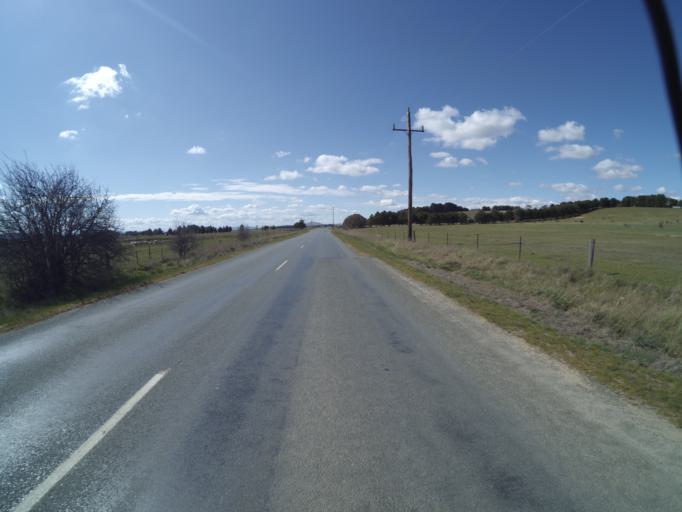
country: AU
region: New South Wales
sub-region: Palerang
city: Bungendore
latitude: -35.2346
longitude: 149.4452
